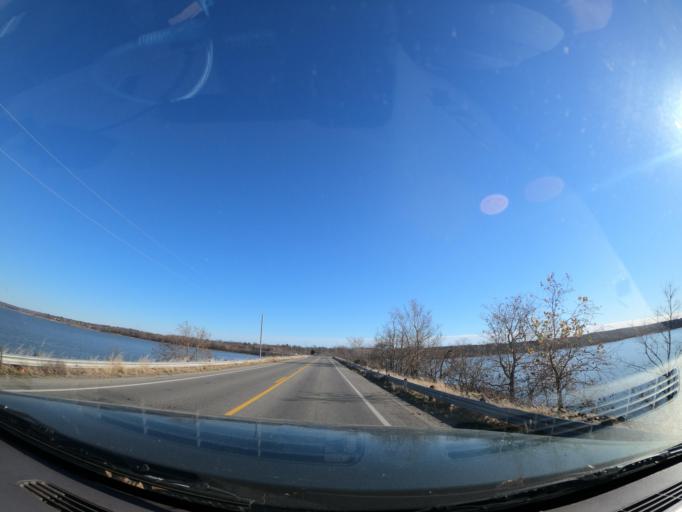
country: US
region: Oklahoma
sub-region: Pittsburg County
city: Longtown
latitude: 35.2419
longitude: -95.5595
